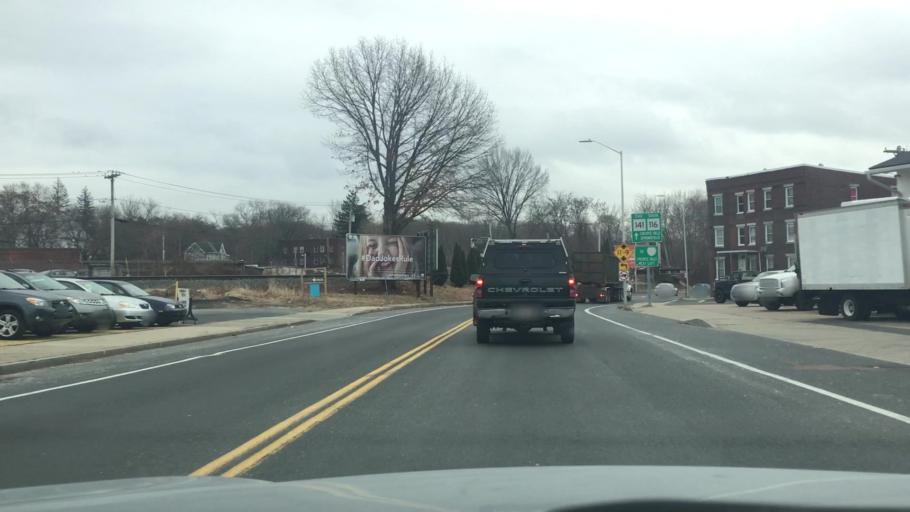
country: US
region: Massachusetts
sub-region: Hampden County
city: North Chicopee
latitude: 42.1938
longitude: -72.6004
